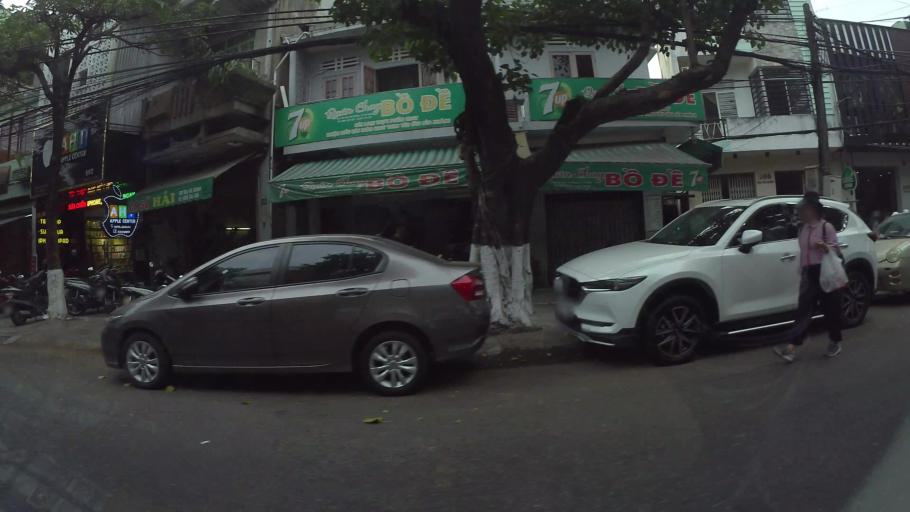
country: VN
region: Da Nang
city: Da Nang
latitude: 16.0621
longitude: 108.2162
